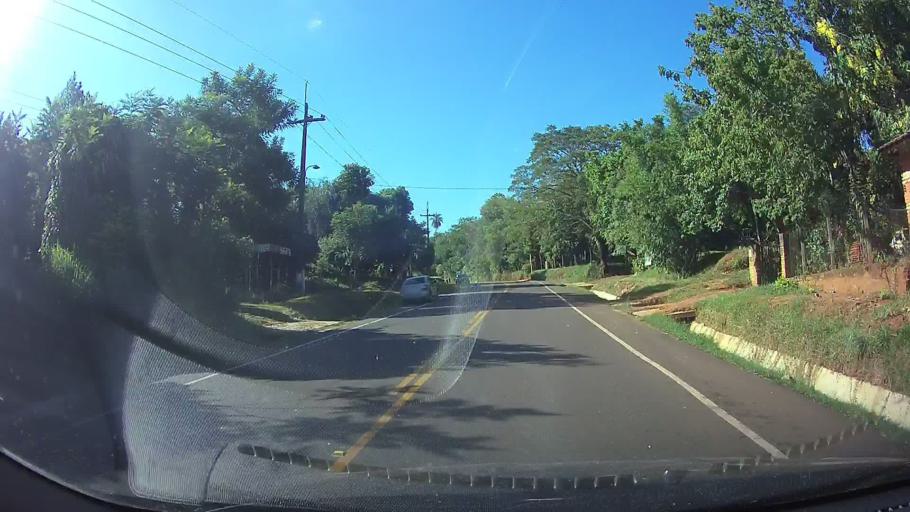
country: PY
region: Cordillera
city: Caacupe
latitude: -25.3496
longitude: -57.1508
